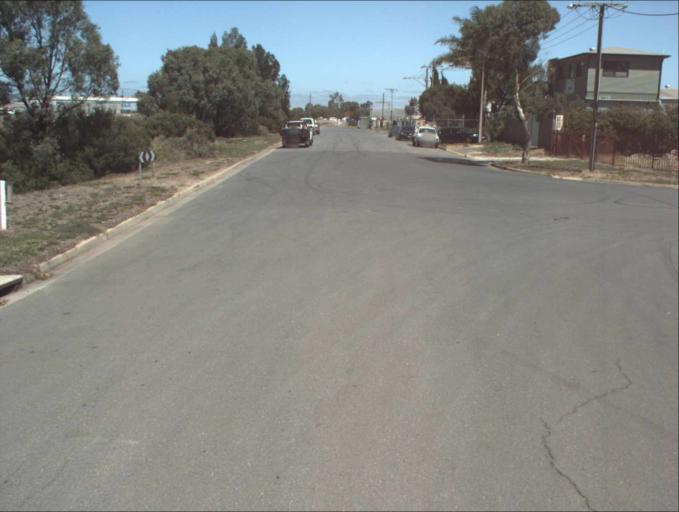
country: AU
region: South Australia
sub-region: Port Adelaide Enfield
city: Blair Athol
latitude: -34.8361
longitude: 138.5681
